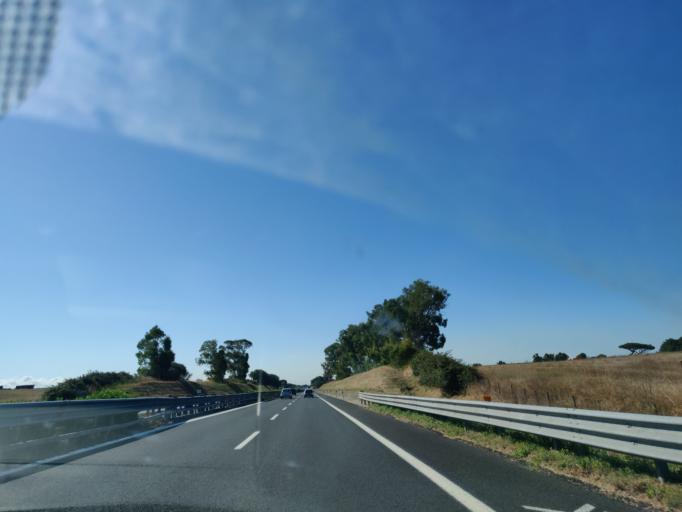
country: IT
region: Latium
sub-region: Citta metropolitana di Roma Capitale
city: Npp 23 (Parco Leonardo)
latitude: 41.8473
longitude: 12.2712
